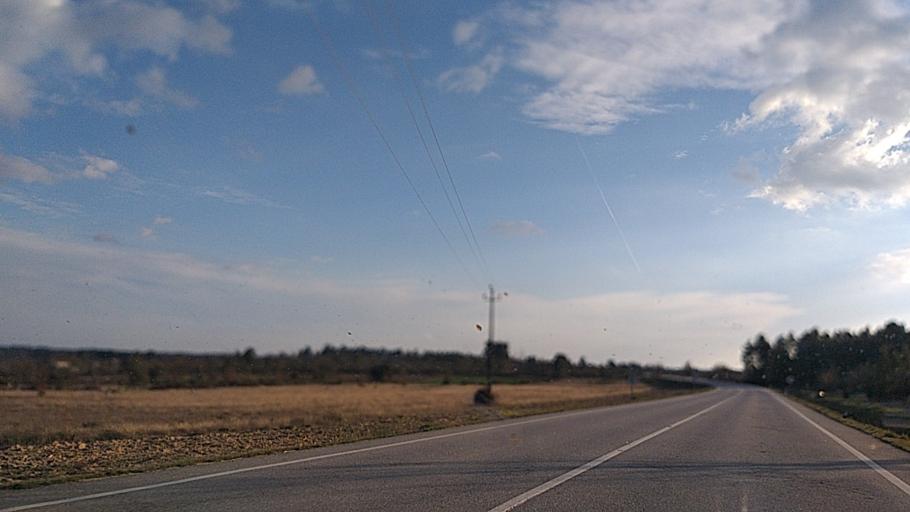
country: PT
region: Guarda
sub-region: Pinhel
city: Pinhel
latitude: 40.6388
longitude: -6.9715
